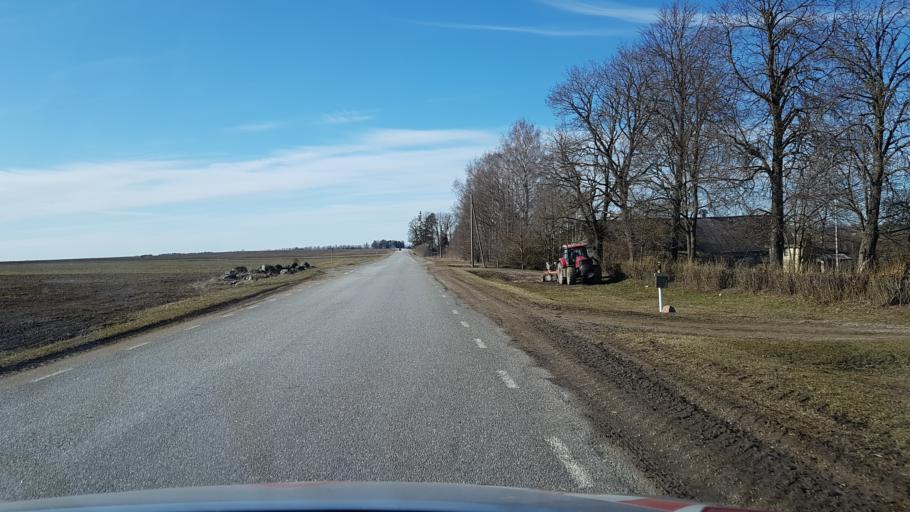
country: EE
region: Laeaene-Virumaa
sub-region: Kadrina vald
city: Kadrina
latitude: 59.3233
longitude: 26.1428
